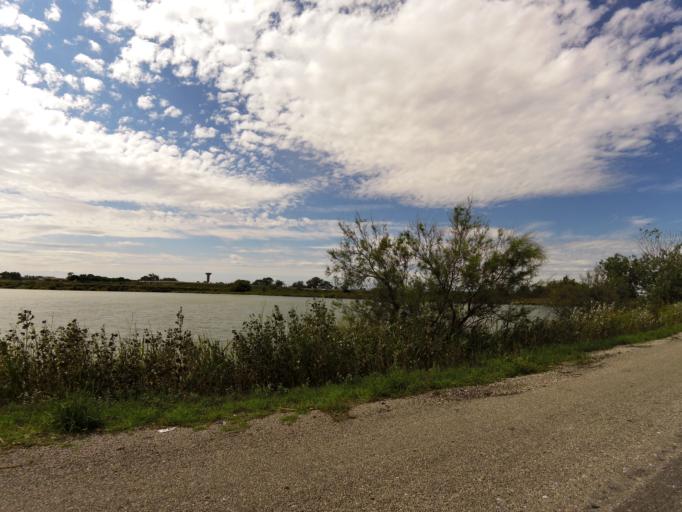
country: FR
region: Languedoc-Roussillon
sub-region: Departement du Gard
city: Le Grau-du-Roi
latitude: 43.5489
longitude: 4.1406
